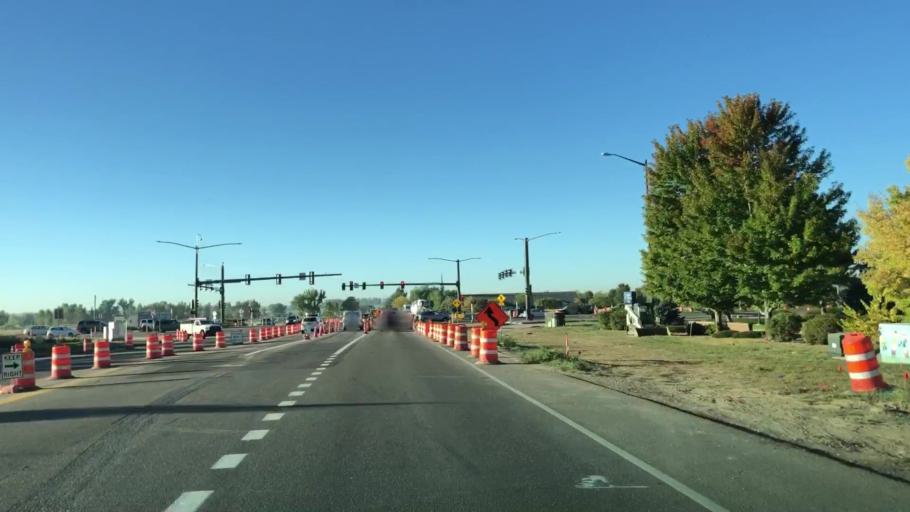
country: US
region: Colorado
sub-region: Larimer County
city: Loveland
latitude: 40.4084
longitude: -105.0211
